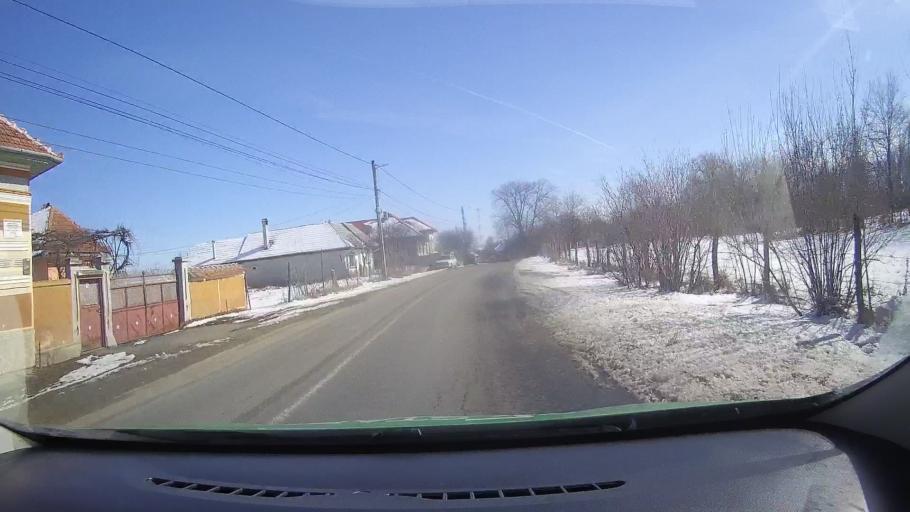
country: RO
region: Brasov
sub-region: Comuna Recea
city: Recea
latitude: 45.7283
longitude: 24.9010
